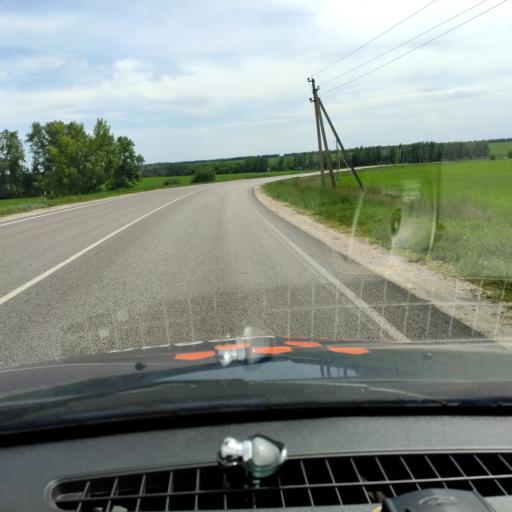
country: RU
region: Voronezj
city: Novaya Usman'
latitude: 51.5575
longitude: 39.3762
